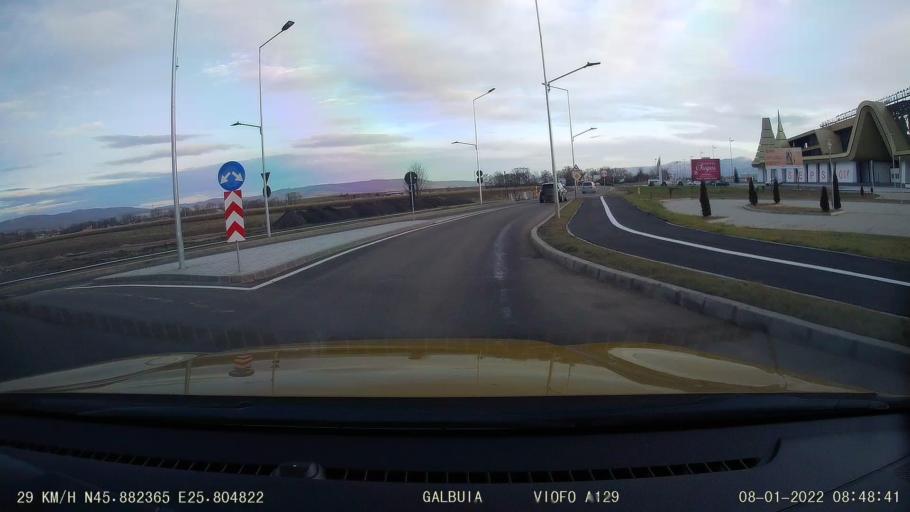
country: RO
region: Covasna
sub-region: Municipiul Sfantu Gheorghe
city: Sfantu-Gheorghe
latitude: 45.8828
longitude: 25.8046
